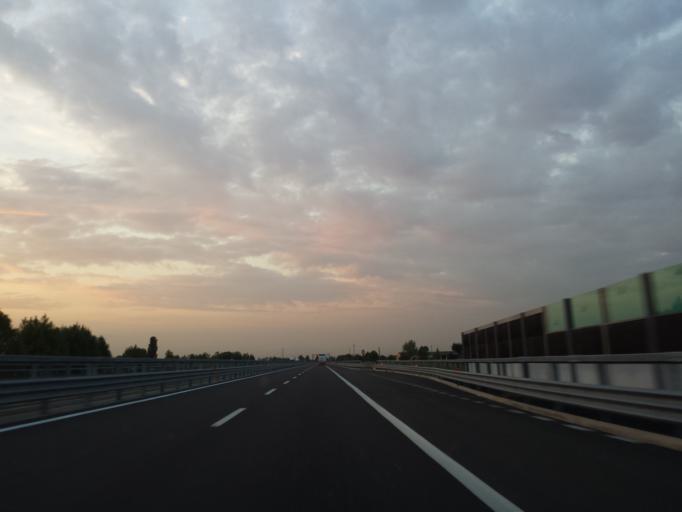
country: IT
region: Veneto
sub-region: Provincia di Vicenza
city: Longare
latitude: 45.4866
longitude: 11.6245
